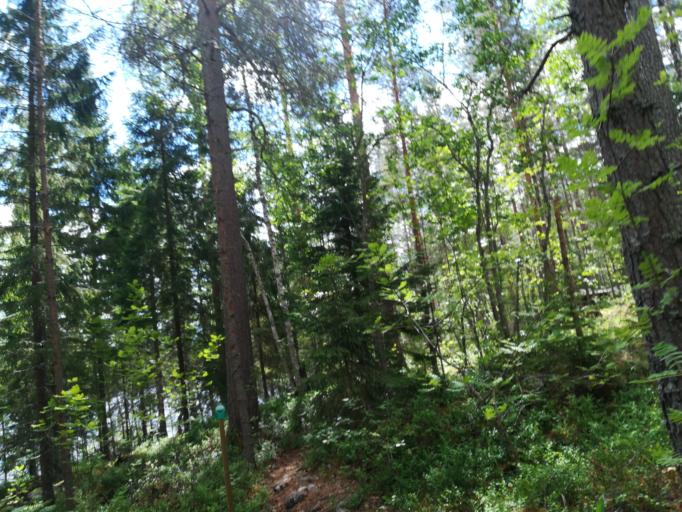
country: FI
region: Southern Savonia
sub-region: Mikkeli
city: Maentyharju
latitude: 61.3636
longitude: 26.9343
